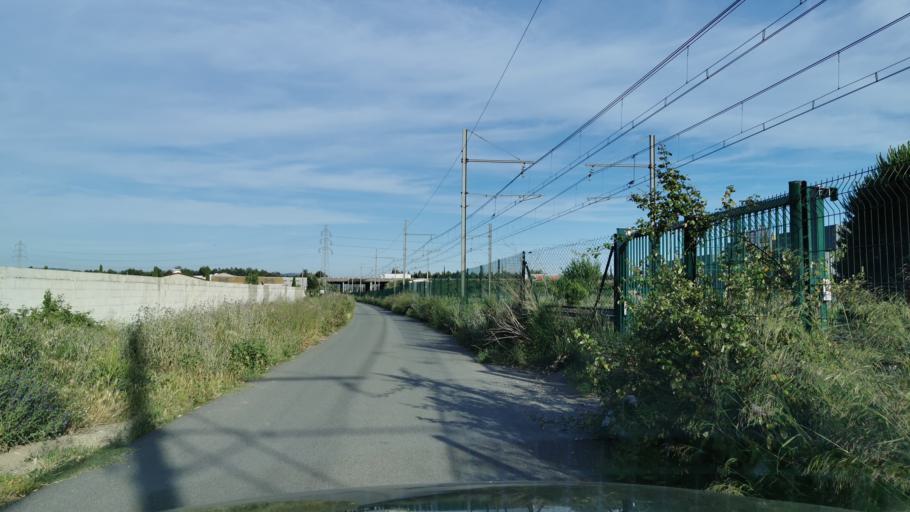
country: FR
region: Languedoc-Roussillon
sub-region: Departement de l'Aude
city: Narbonne
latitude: 43.1674
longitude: 2.9960
